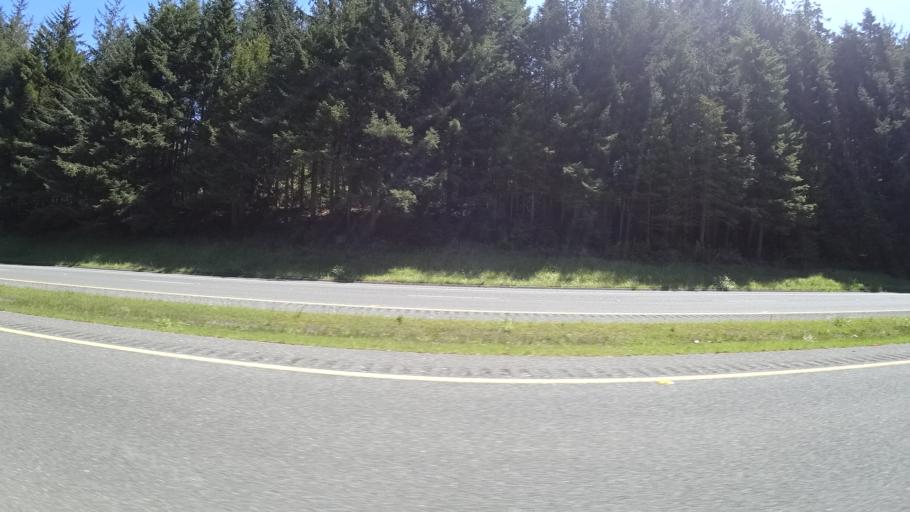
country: US
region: California
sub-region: Humboldt County
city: Westhaven-Moonstone
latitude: 41.1039
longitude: -124.1546
